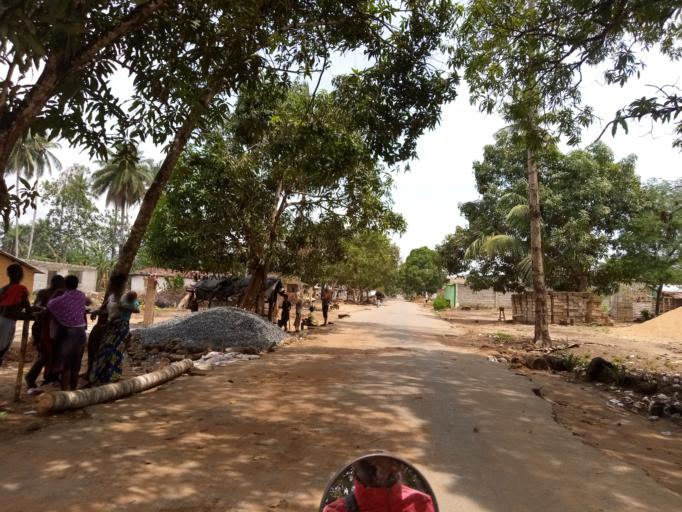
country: SL
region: Western Area
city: Waterloo
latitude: 8.3341
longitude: -13.0169
